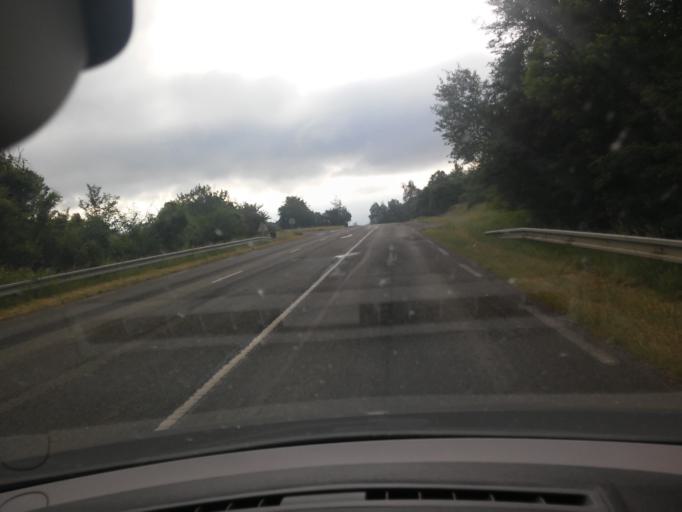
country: FR
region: Lorraine
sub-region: Departement de la Moselle
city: Rozerieulles
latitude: 49.1078
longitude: 6.0630
